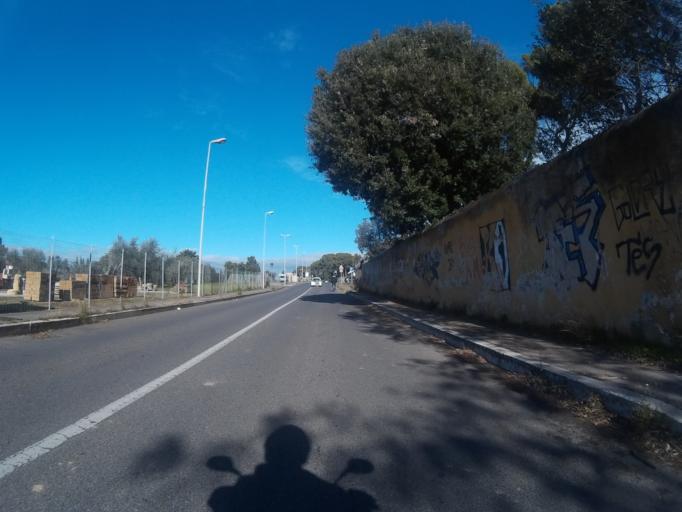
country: IT
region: Tuscany
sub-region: Provincia di Livorno
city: Livorno
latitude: 43.5215
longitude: 10.3463
